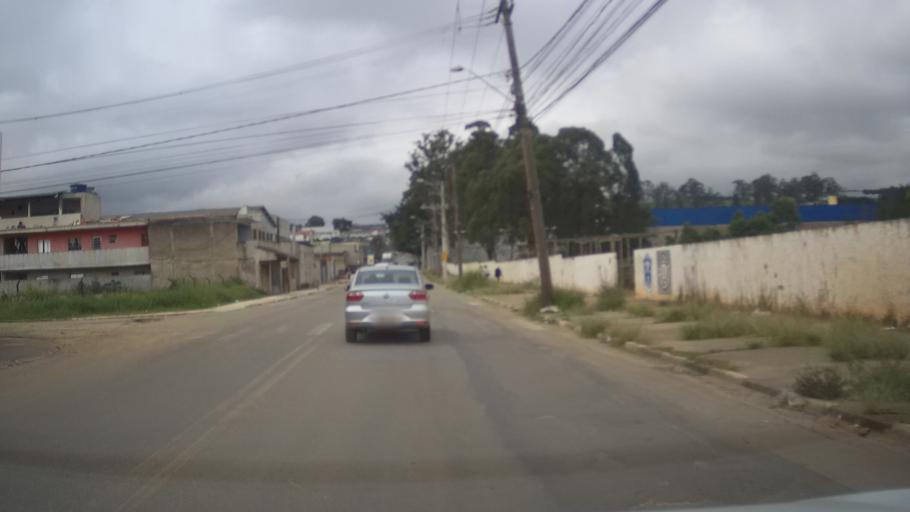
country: BR
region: Sao Paulo
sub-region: Aruja
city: Aruja
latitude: -23.4135
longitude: -46.3855
